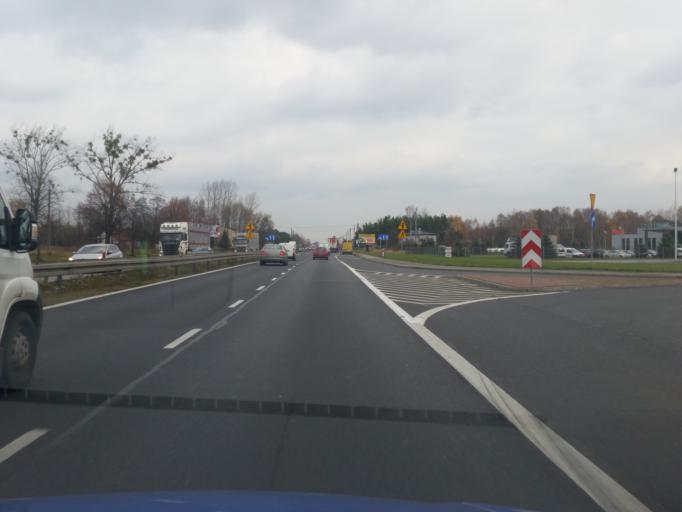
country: PL
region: Silesian Voivodeship
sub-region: Powiat czestochowski
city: Kamienica Polska
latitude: 50.6865
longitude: 19.1324
